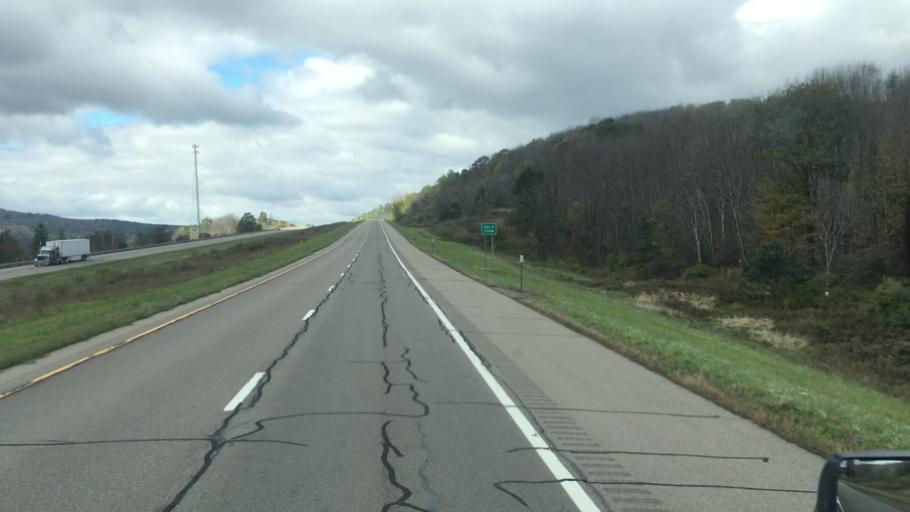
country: US
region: New York
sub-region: Allegany County
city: Friendship
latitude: 42.2082
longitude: -78.1907
